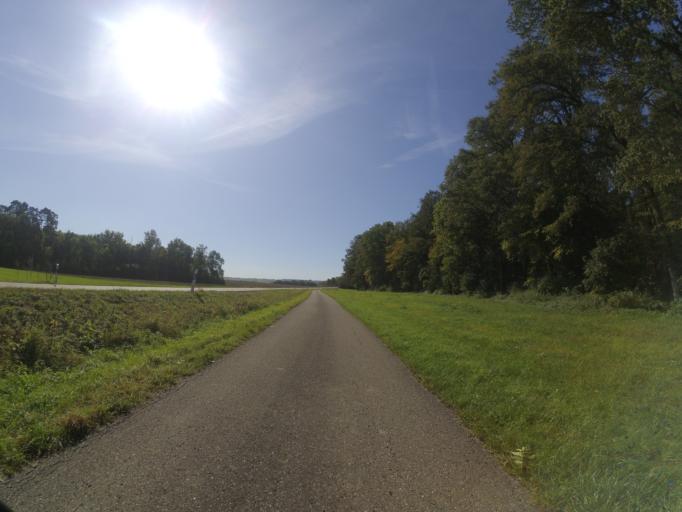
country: DE
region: Baden-Wuerttemberg
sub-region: Tuebingen Region
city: Nerenstetten
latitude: 48.5133
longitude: 10.0840
